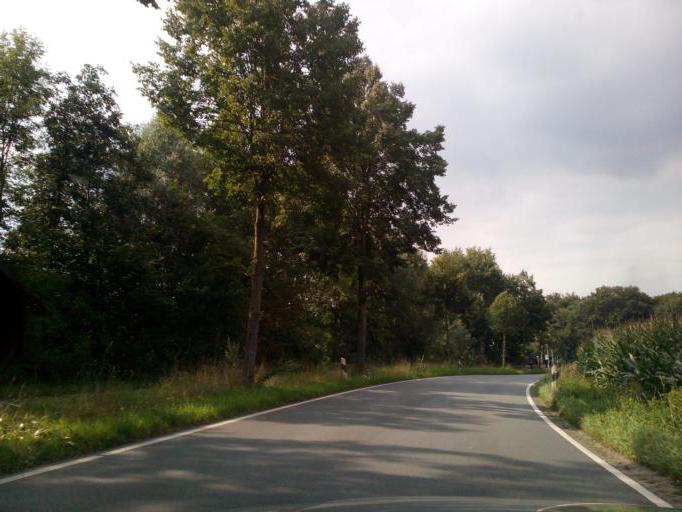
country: DE
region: North Rhine-Westphalia
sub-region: Regierungsbezirk Munster
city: Muenster
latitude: 51.9149
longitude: 7.6166
